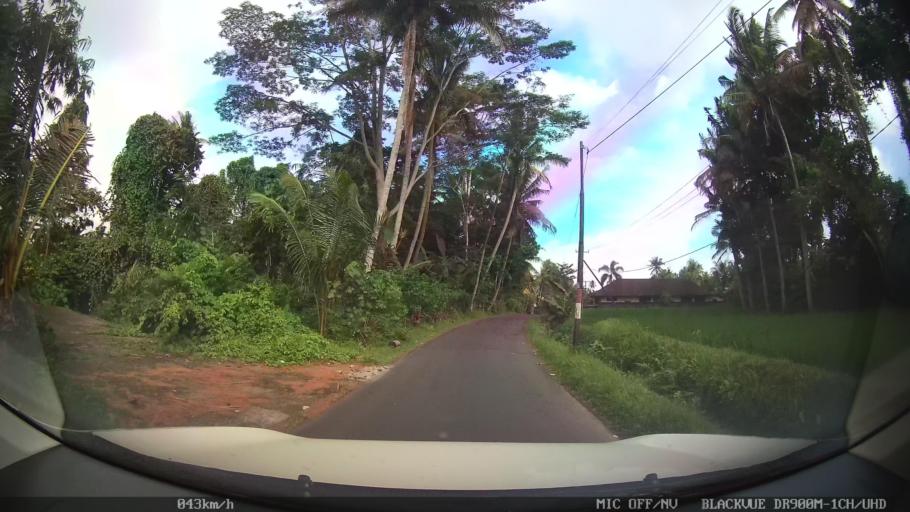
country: ID
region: Bali
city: Banjar Pesalakan
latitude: -8.4868
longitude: 115.2978
